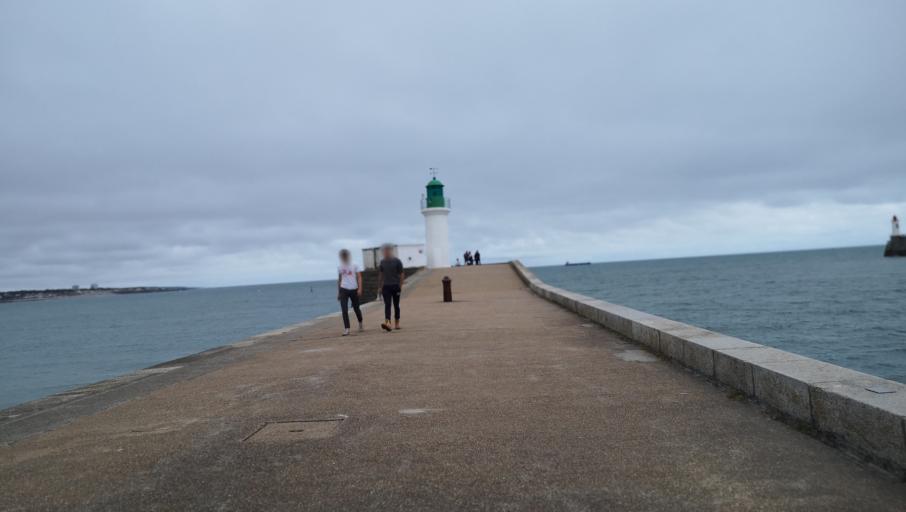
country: FR
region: Pays de la Loire
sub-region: Departement de la Vendee
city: Les Sables-d'Olonne
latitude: 46.4912
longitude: -1.7924
